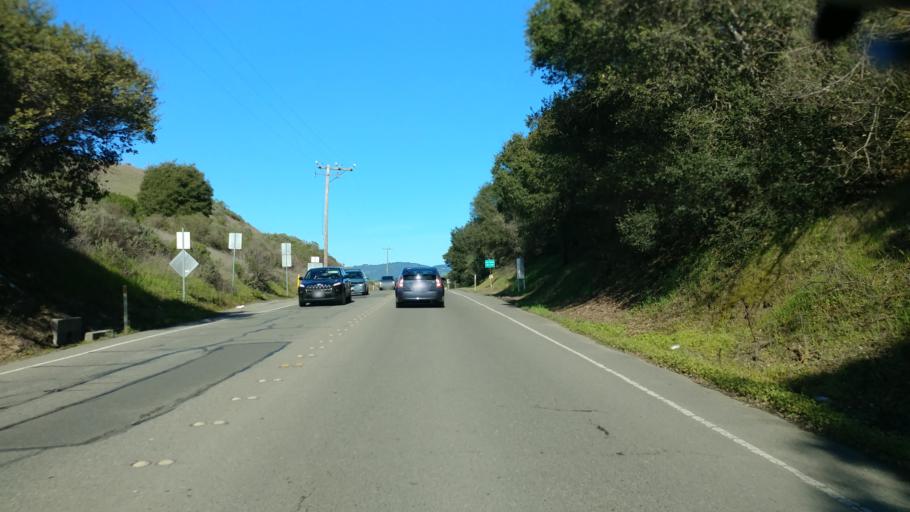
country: US
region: California
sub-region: Contra Costa County
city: San Ramon
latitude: 37.7698
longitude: -122.0047
